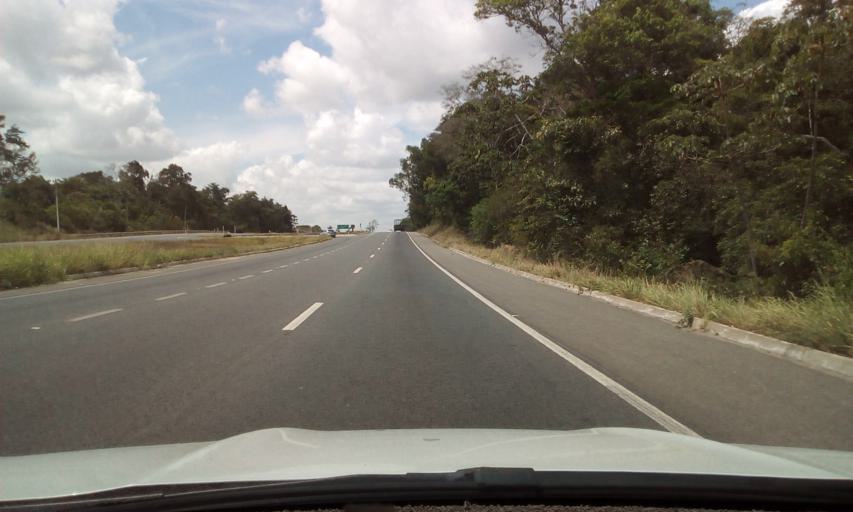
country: BR
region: Paraiba
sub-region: Santa Rita
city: Santa Rita
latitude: -7.1441
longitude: -34.9976
